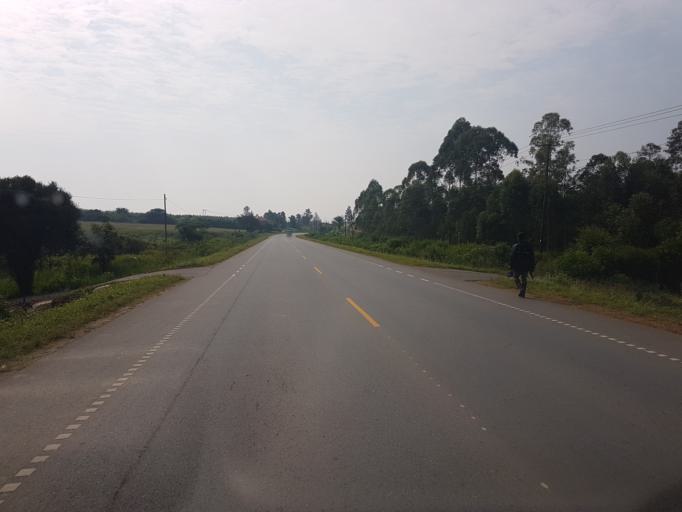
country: UG
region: Western Region
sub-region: Sheema District
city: Kibingo
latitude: -0.6348
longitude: 30.5339
